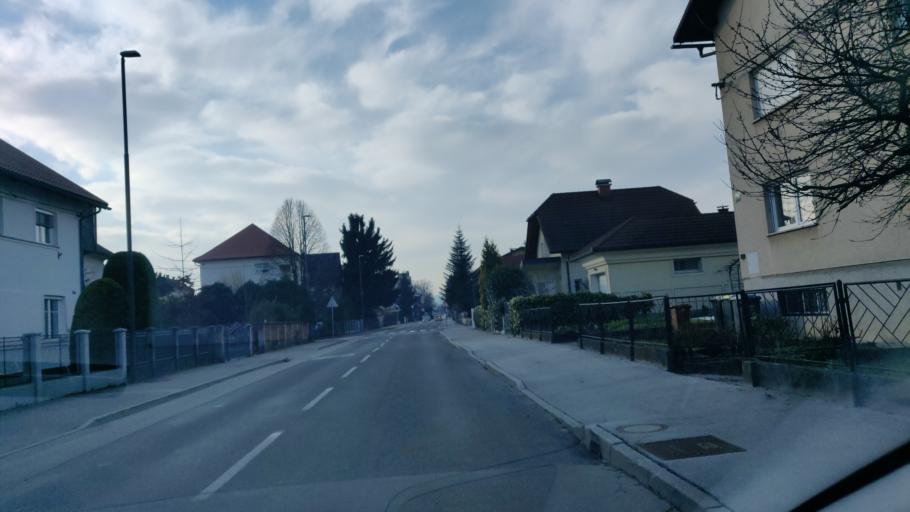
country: SI
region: Ljubljana
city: Ljubljana
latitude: 46.0403
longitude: 14.4925
